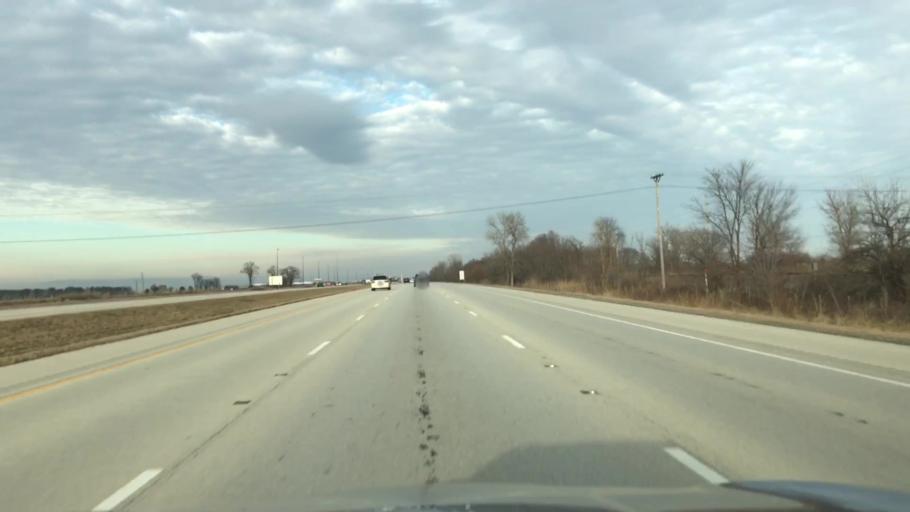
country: US
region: Illinois
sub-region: Sangamon County
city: Sherman
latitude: 39.9223
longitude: -89.5779
